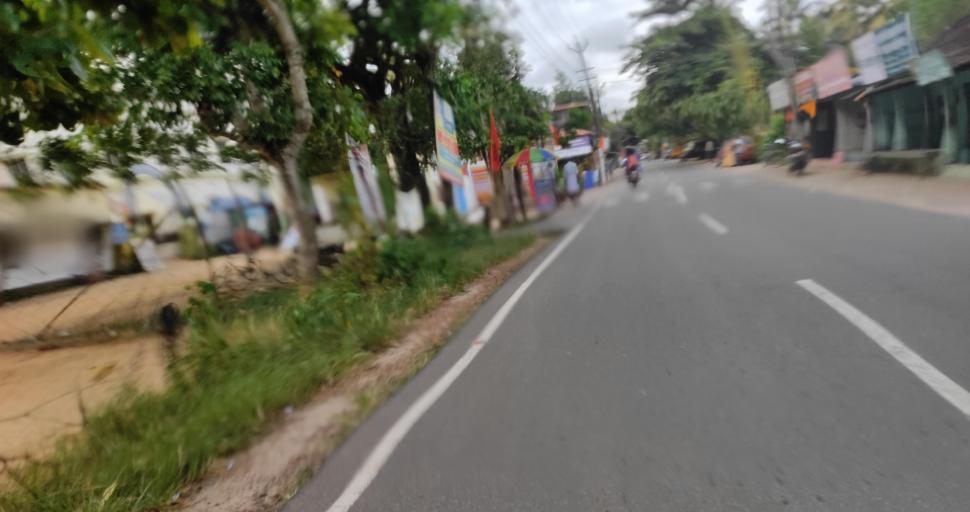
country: IN
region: Kerala
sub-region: Alappuzha
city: Shertallai
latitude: 9.6546
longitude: 76.3179
